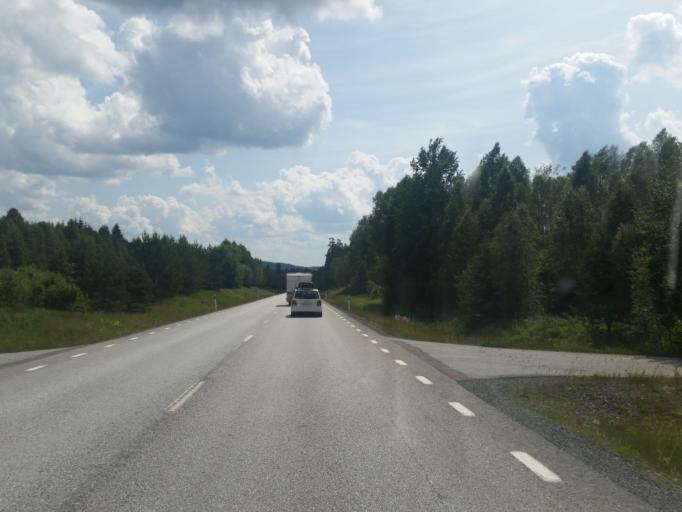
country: SE
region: OErebro
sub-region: Ljusnarsbergs Kommun
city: Kopparberg
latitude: 59.8809
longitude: 15.0290
